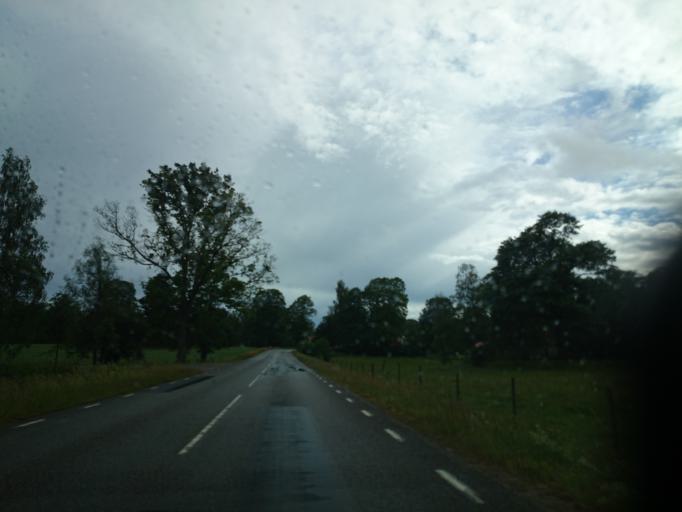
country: SE
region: Joenkoeping
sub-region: Varnamo Kommun
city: Varnamo
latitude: 57.0804
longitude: 13.9463
